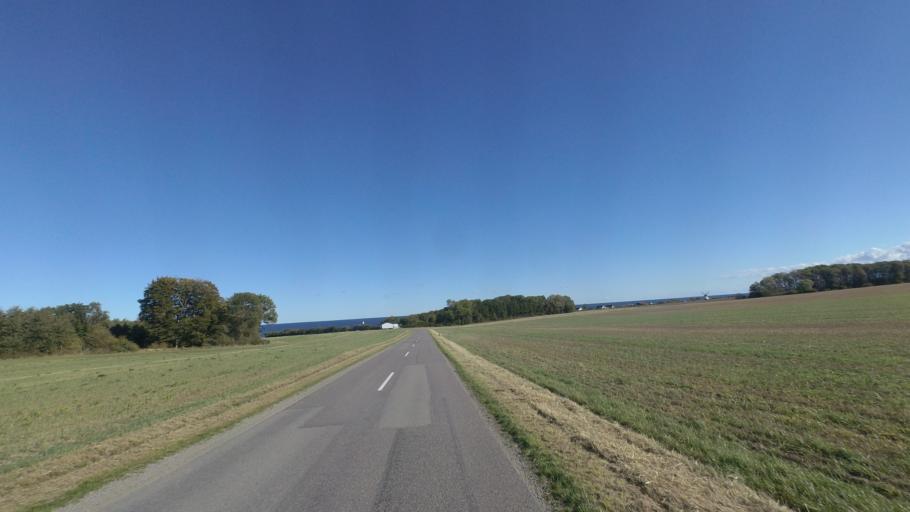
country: DK
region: Capital Region
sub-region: Bornholm Kommune
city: Nexo
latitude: 55.1105
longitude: 15.1320
